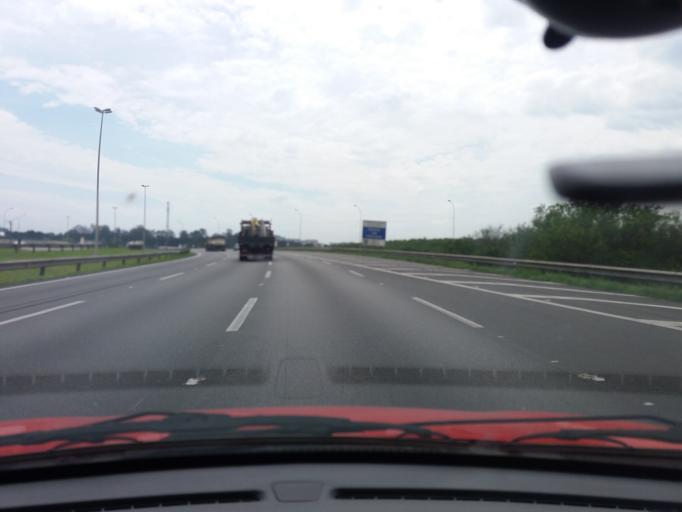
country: BR
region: Sao Paulo
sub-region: Carapicuiba
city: Carapicuiba
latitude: -23.5177
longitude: -46.8154
